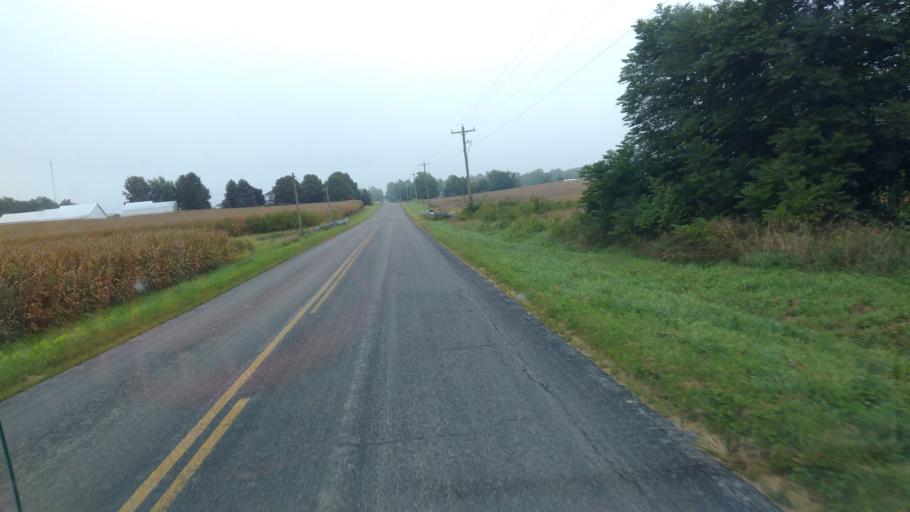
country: US
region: Ohio
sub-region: Union County
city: Richwood
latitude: 40.4897
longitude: -83.3795
